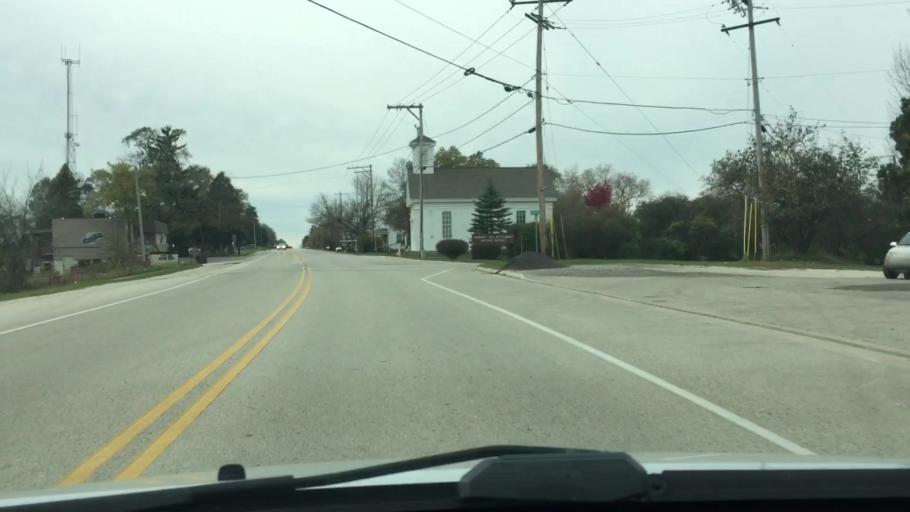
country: US
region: Wisconsin
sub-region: Waukesha County
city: Muskego
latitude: 42.9448
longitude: -88.1593
